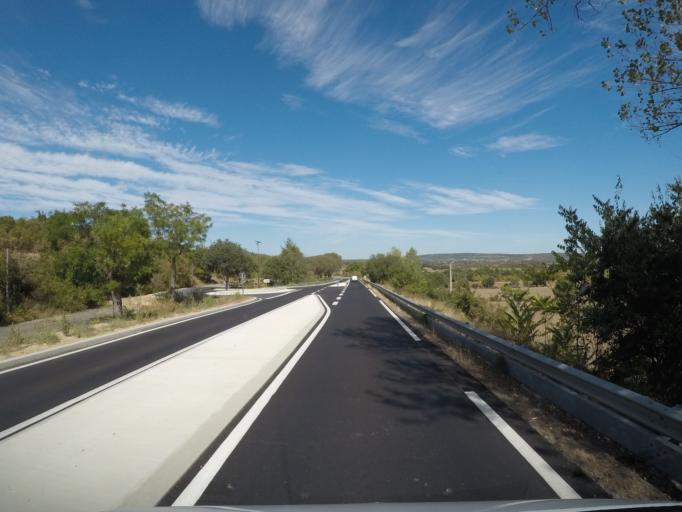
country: FR
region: Languedoc-Roussillon
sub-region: Departement de l'Herault
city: Saint-Martin-de-Londres
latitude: 43.8066
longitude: 3.7399
